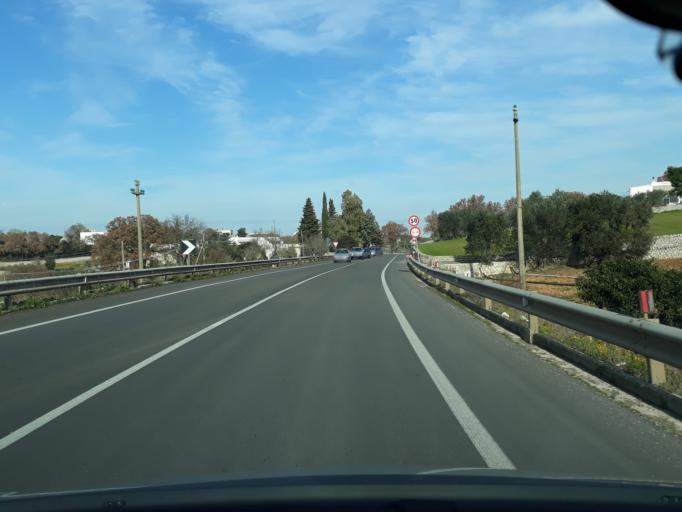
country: IT
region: Apulia
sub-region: Provincia di Bari
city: Locorotondo
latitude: 40.7837
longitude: 17.3396
